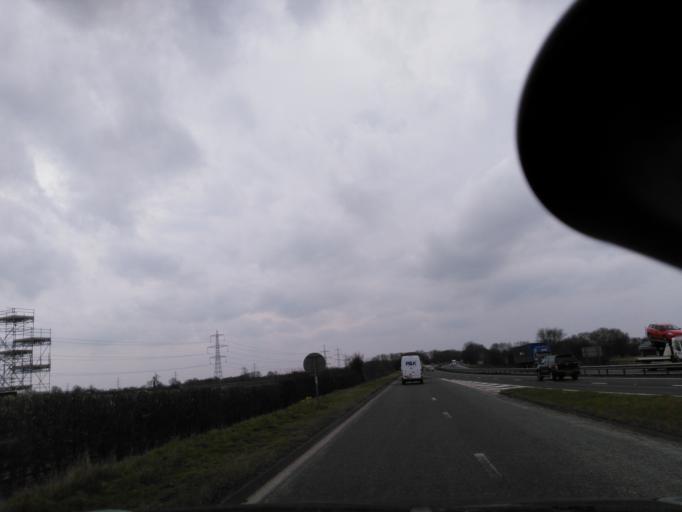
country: GB
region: England
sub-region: North Yorkshire
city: Thirsk
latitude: 54.2233
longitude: -1.3287
